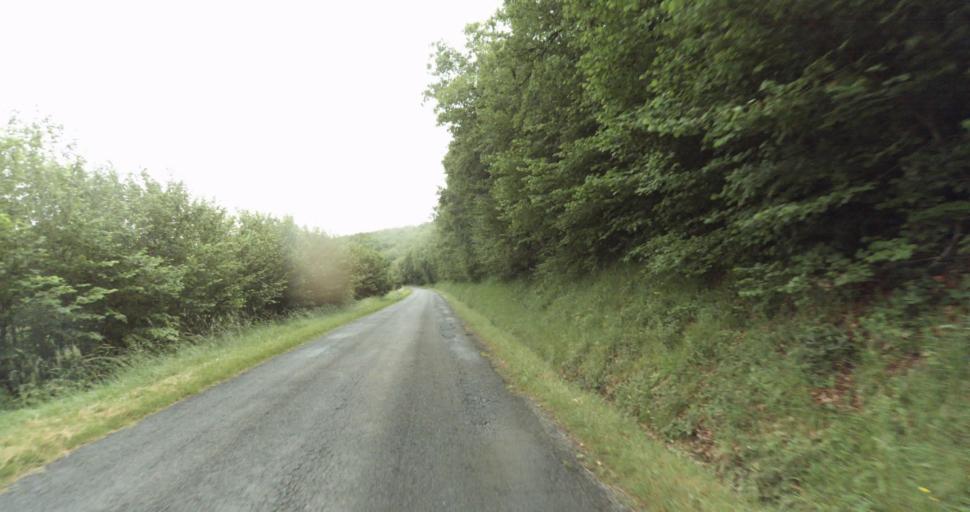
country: FR
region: Aquitaine
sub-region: Departement de la Dordogne
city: Beaumont-du-Perigord
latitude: 44.7582
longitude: 0.8099
